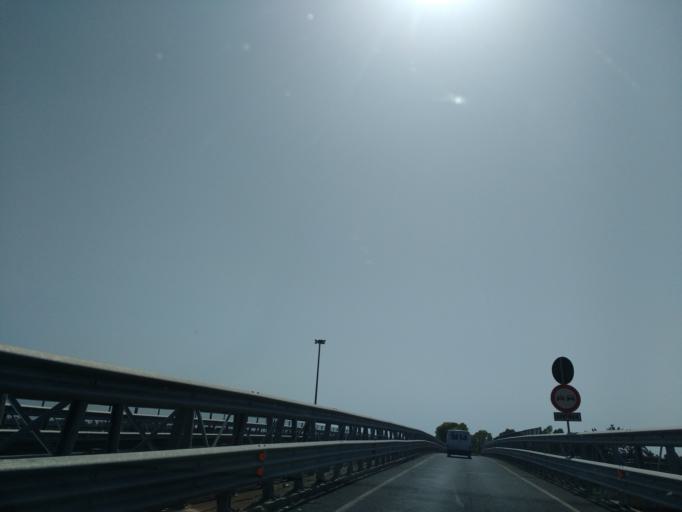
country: IT
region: Sicily
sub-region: Catania
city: Catania
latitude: 37.4797
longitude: 15.0633
